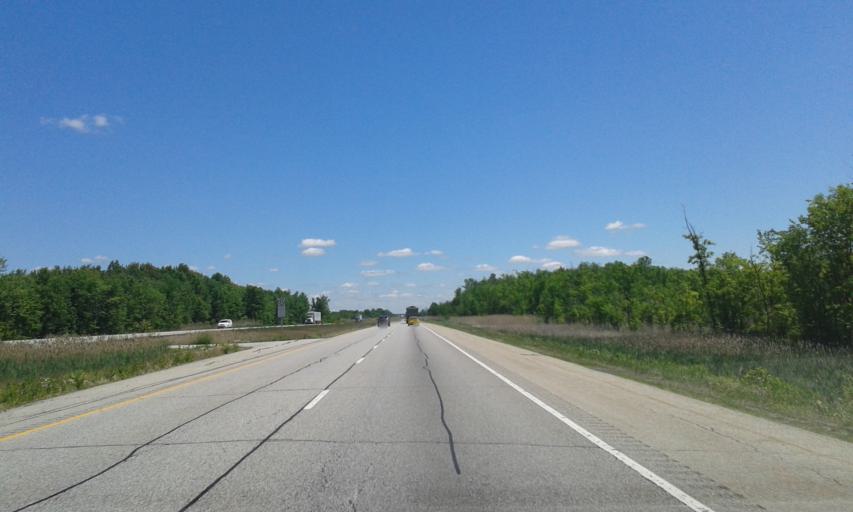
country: US
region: New York
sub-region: St. Lawrence County
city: Norfolk
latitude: 44.9108
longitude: -75.2122
